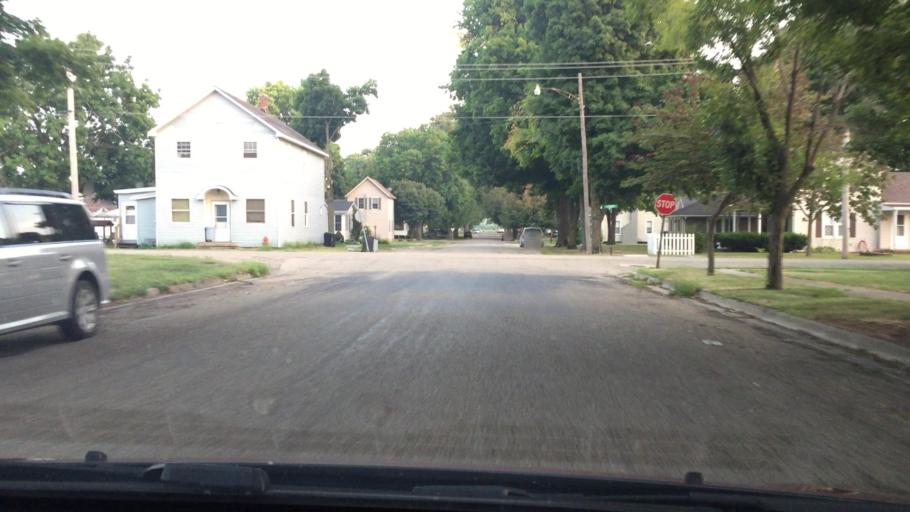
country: US
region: Illinois
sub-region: Bureau County
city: Ladd
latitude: 41.3829
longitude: -89.2204
